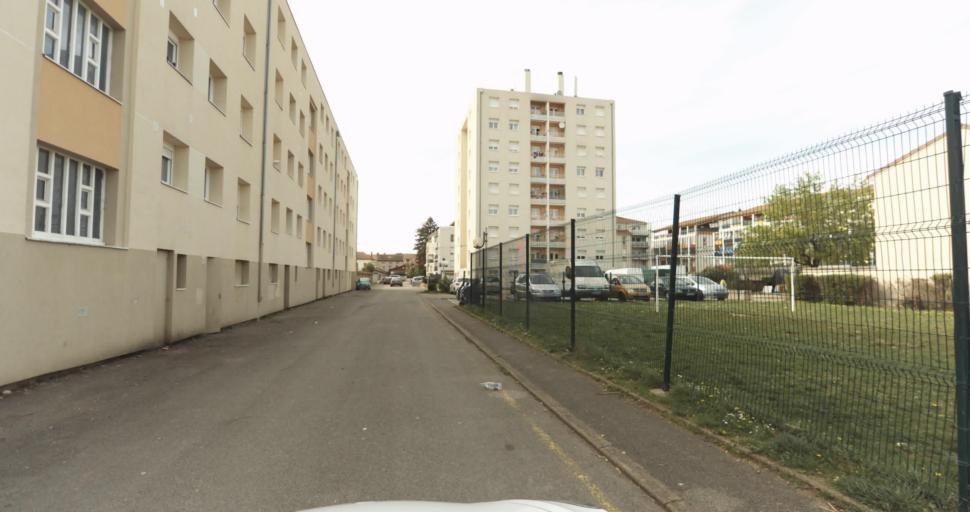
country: FR
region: Rhone-Alpes
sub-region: Departement de l'Ain
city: Amberieu-en-Bugey
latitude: 45.9538
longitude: 5.3465
